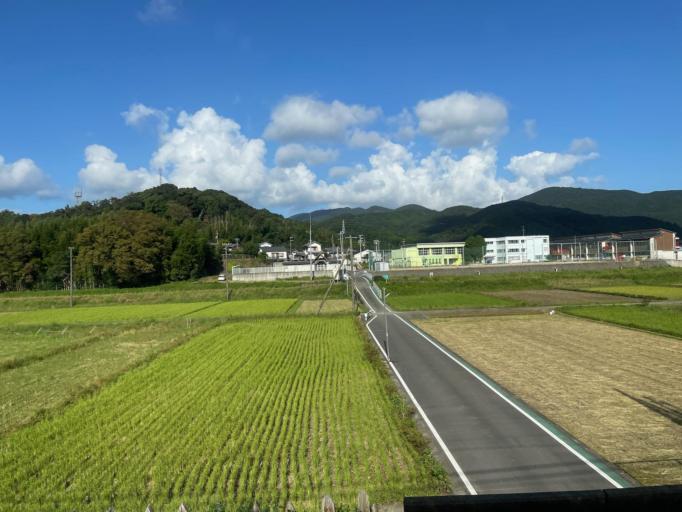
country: JP
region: Mie
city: Toba
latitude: 34.4438
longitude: 136.8464
